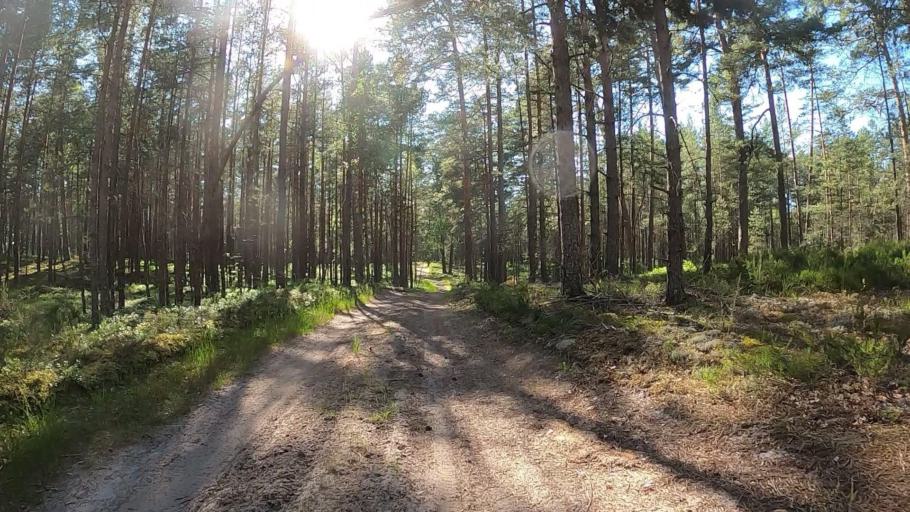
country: LV
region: Carnikava
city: Carnikava
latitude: 57.0990
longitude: 24.2383
